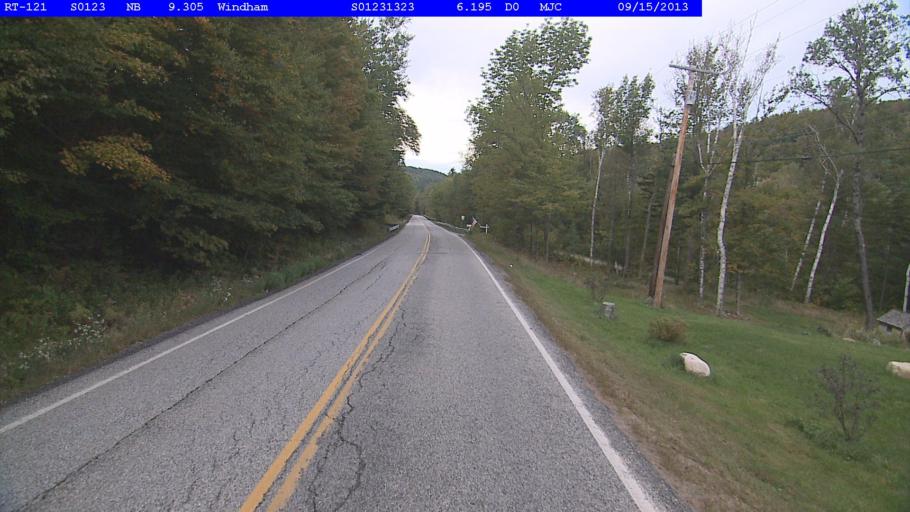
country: US
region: Vermont
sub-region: Windsor County
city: Chester
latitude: 43.2053
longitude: -72.7332
